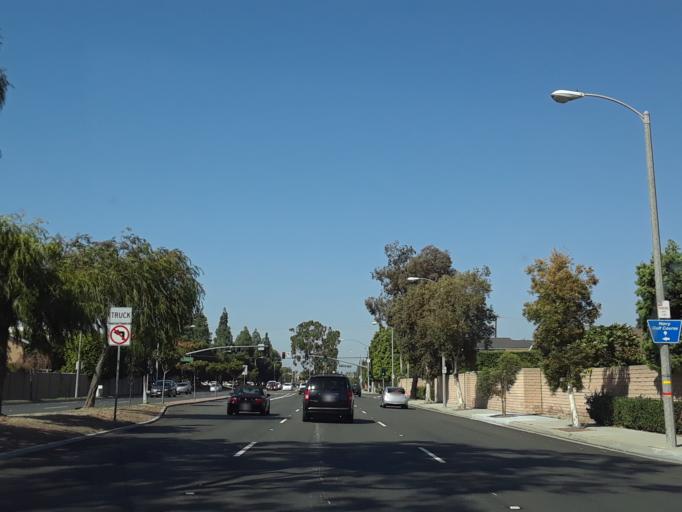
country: US
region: California
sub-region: Orange County
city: Cypress
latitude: 33.7944
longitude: -118.0284
